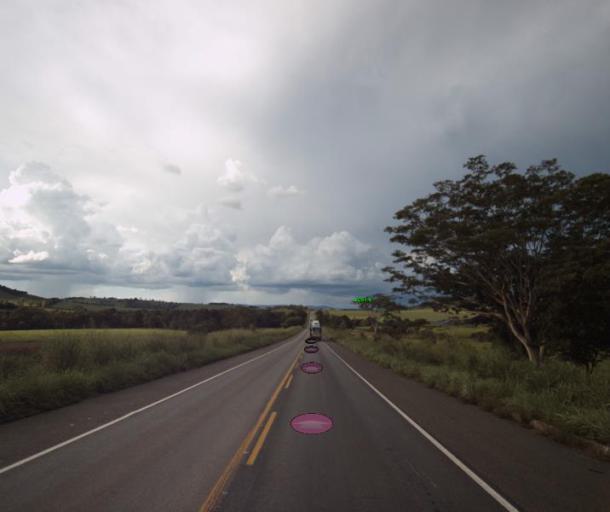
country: BR
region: Goias
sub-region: Ceres
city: Ceres
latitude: -15.2371
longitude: -49.5560
